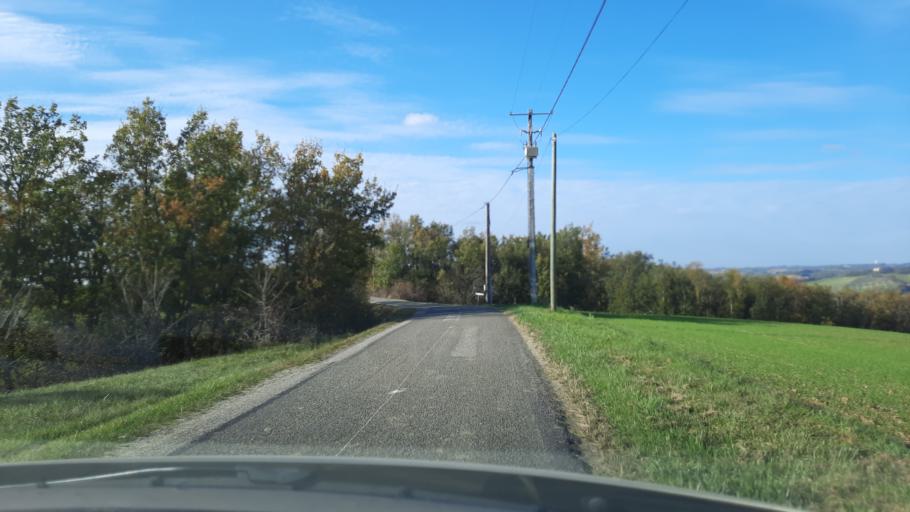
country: FR
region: Midi-Pyrenees
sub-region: Departement du Tarn-et-Garonne
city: Lafrancaise
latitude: 44.1478
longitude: 1.2996
